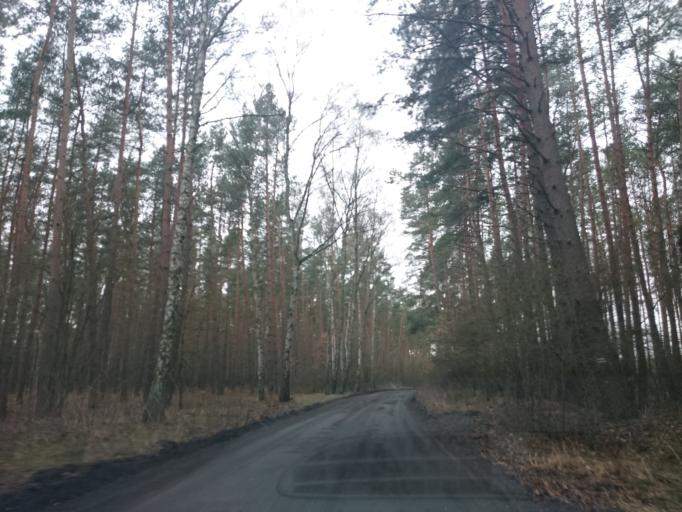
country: PL
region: Kujawsko-Pomorskie
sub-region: Powiat golubsko-dobrzynski
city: Ciechocin
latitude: 53.0688
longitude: 18.8867
